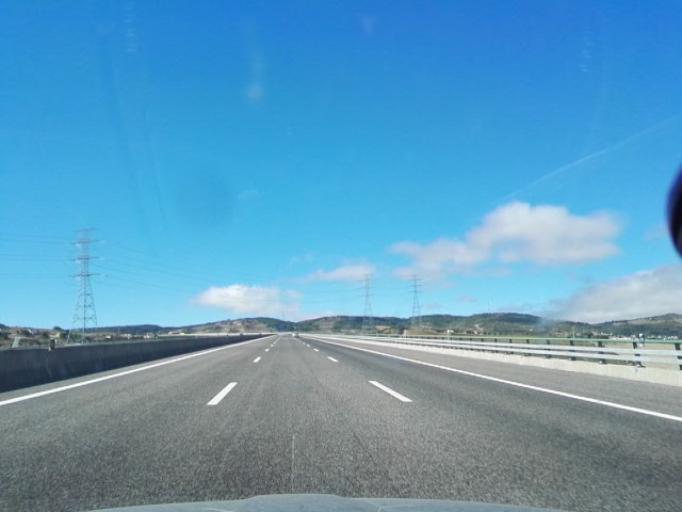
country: PT
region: Lisbon
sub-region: Arruda Dos Vinhos
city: Arruda dos Vinhos
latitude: 38.9834
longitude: -9.0533
